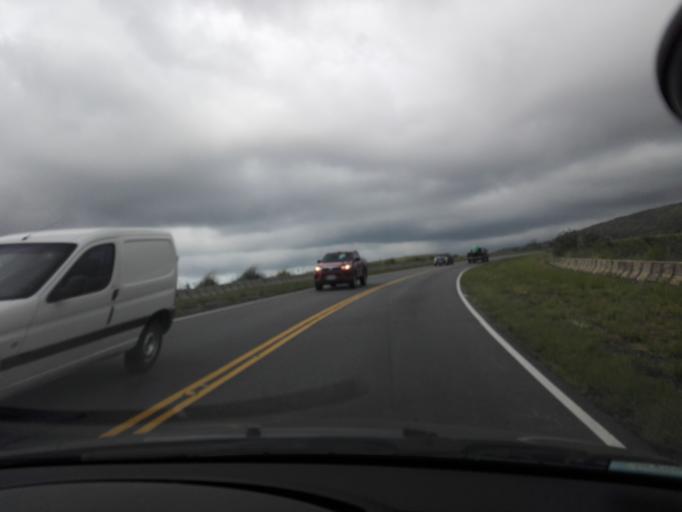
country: AR
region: Cordoba
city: Cuesta Blanca
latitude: -31.6040
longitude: -64.6737
